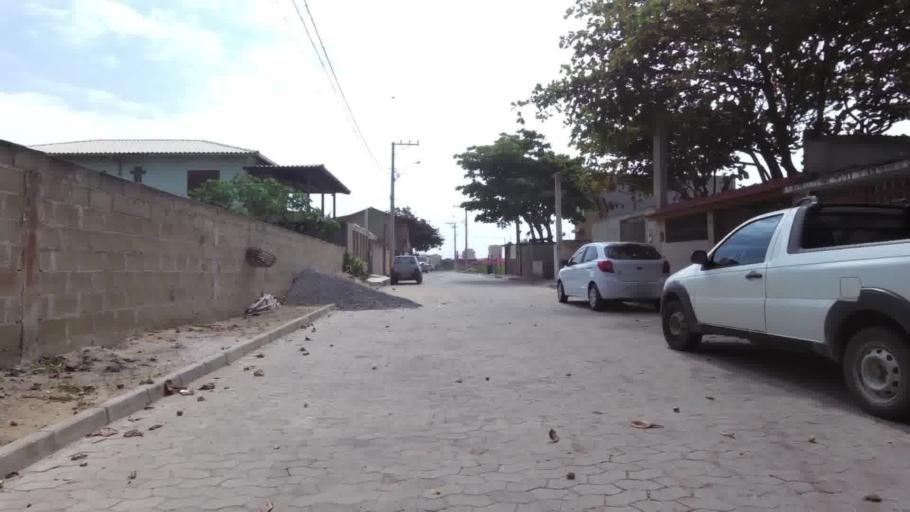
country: BR
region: Espirito Santo
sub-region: Marataizes
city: Marataizes
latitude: -21.0257
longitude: -40.8125
